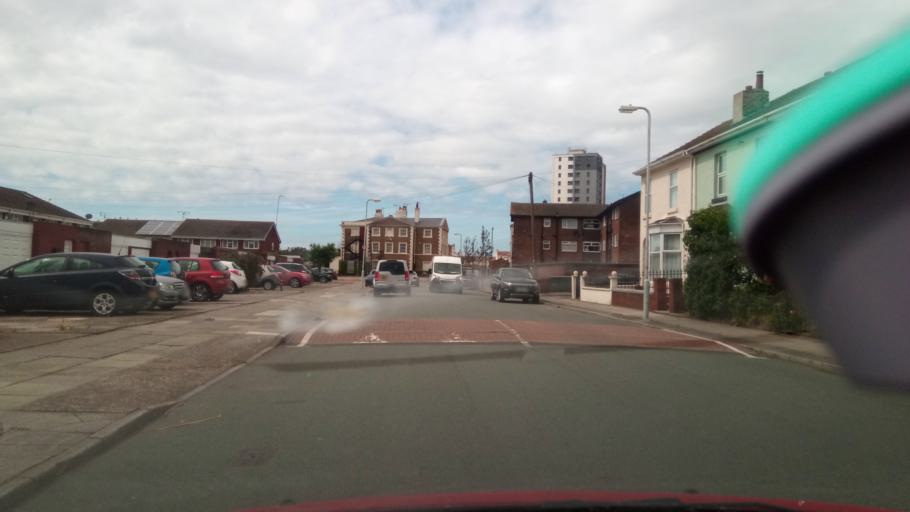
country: GB
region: England
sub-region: Sefton
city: Waterloo
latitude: 53.4707
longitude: -3.0259
